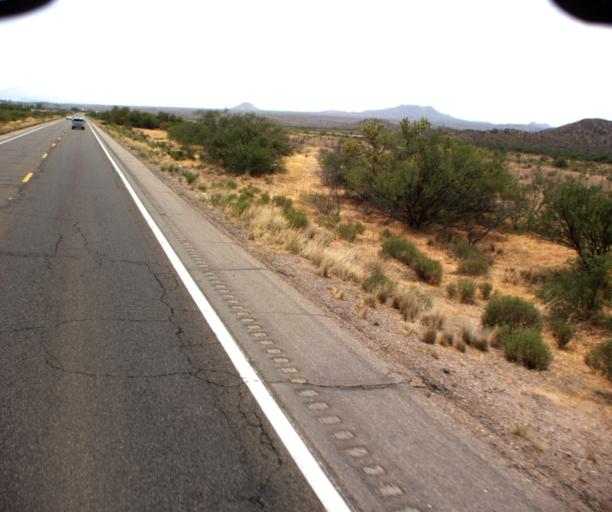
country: US
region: Arizona
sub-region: Gila County
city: Globe
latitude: 33.3575
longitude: -110.6819
